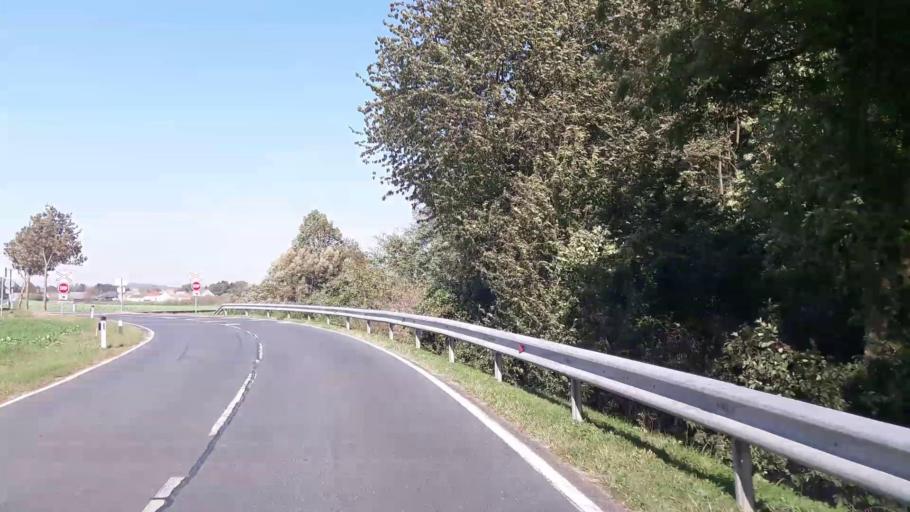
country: AT
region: Lower Austria
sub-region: Politischer Bezirk Korneuburg
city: Ernstbrunn
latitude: 48.4902
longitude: 16.3703
